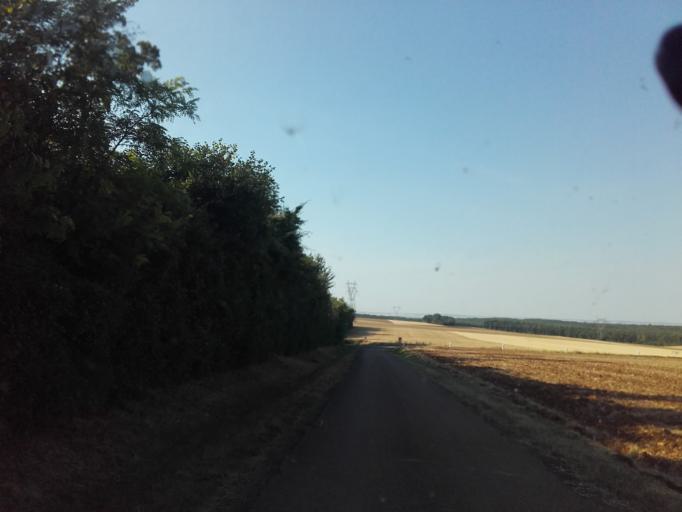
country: FR
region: Bourgogne
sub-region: Departement de l'Yonne
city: Chablis
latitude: 47.8380
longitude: 3.8441
